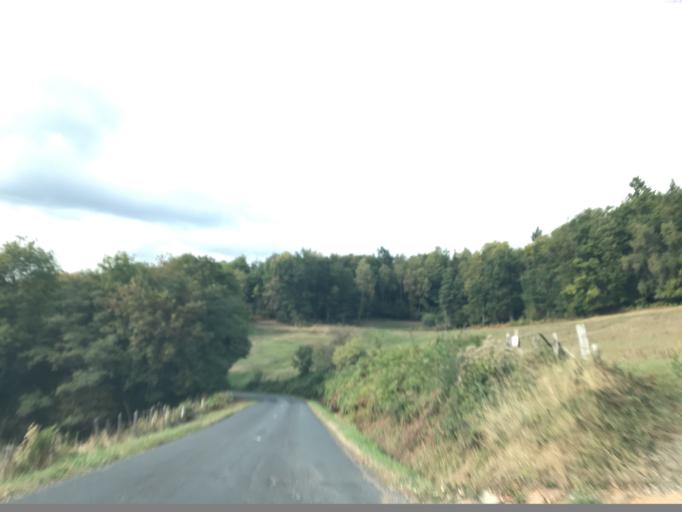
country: FR
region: Auvergne
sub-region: Departement du Puy-de-Dome
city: Escoutoux
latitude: 45.7856
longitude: 3.6191
